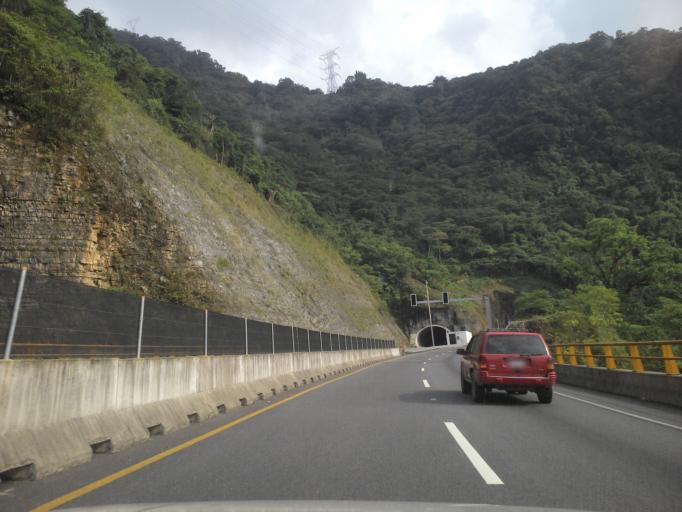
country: MX
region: Puebla
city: Xicotepec de Juarez
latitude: 20.3178
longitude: -97.9638
